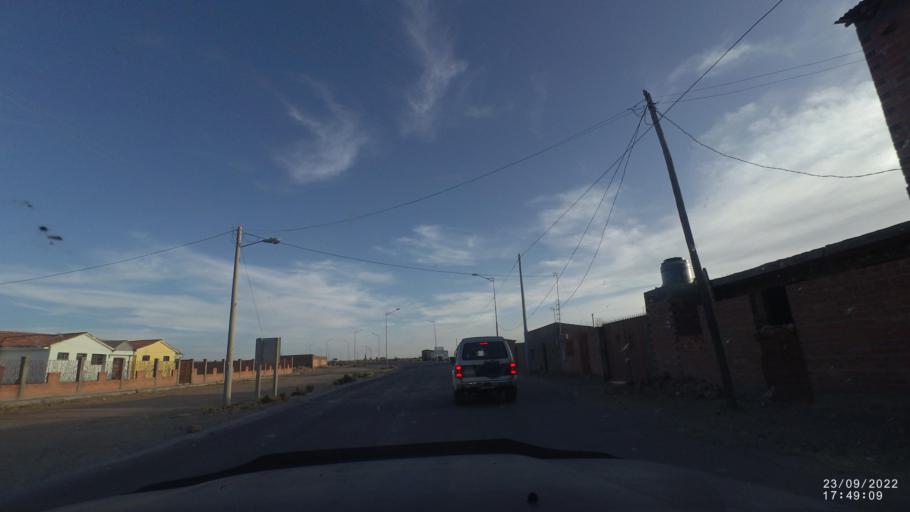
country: BO
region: Oruro
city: Challapata
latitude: -19.0199
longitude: -66.7776
